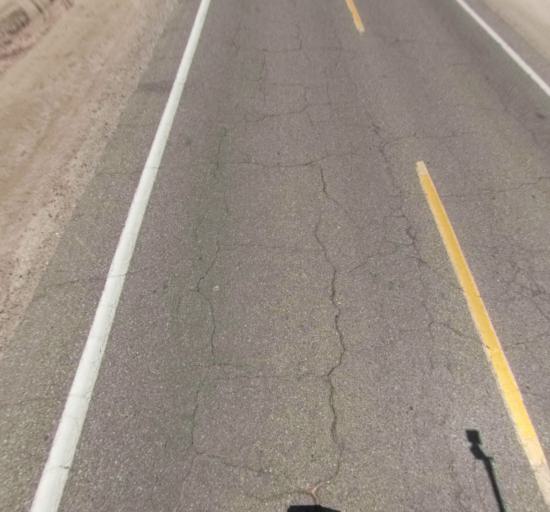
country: US
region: California
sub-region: Madera County
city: Fairmead
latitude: 36.9583
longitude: -120.2021
